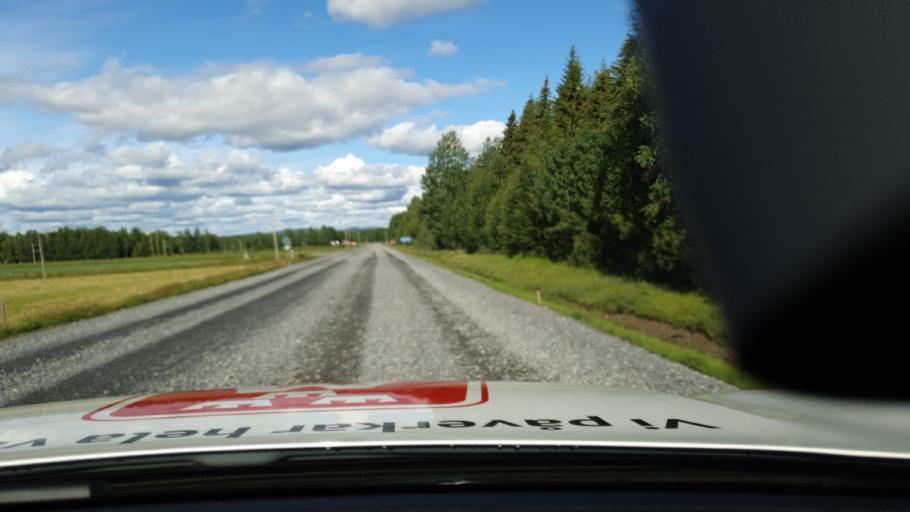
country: SE
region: Norrbotten
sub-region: Bodens Kommun
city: Boden
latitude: 65.8505
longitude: 21.5264
